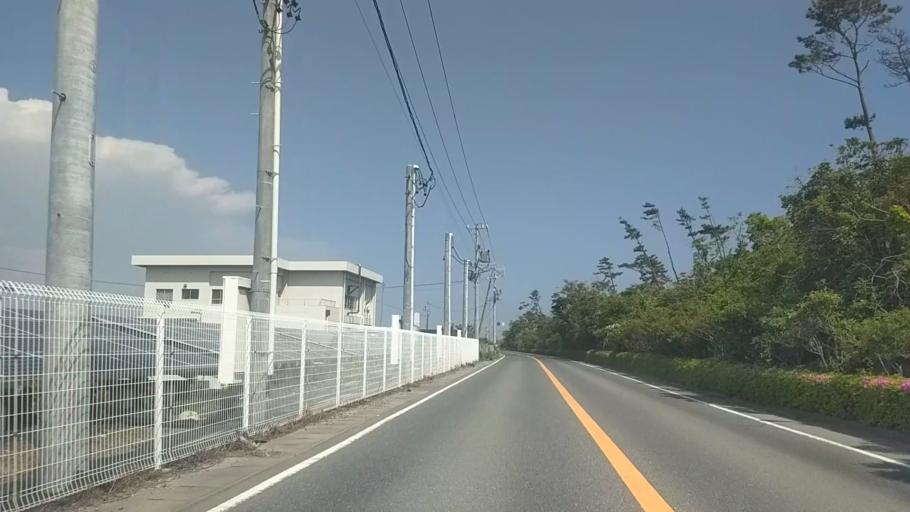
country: JP
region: Shizuoka
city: Hamamatsu
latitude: 34.6689
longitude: 137.7014
